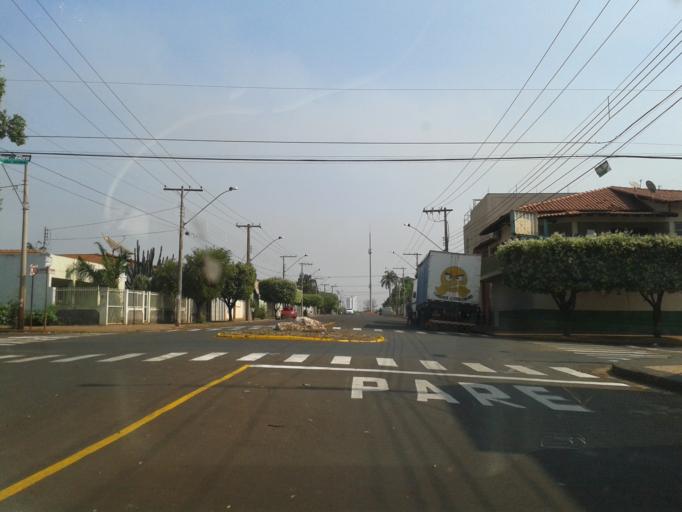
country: BR
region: Minas Gerais
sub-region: Ituiutaba
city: Ituiutaba
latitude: -18.9656
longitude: -49.4499
